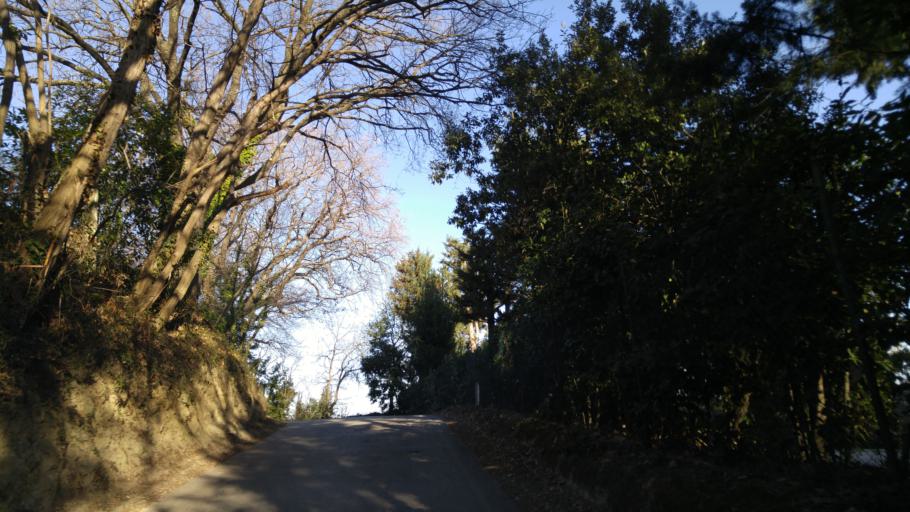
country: IT
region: The Marches
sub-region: Provincia di Pesaro e Urbino
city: Fenile
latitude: 43.8518
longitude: 12.9261
